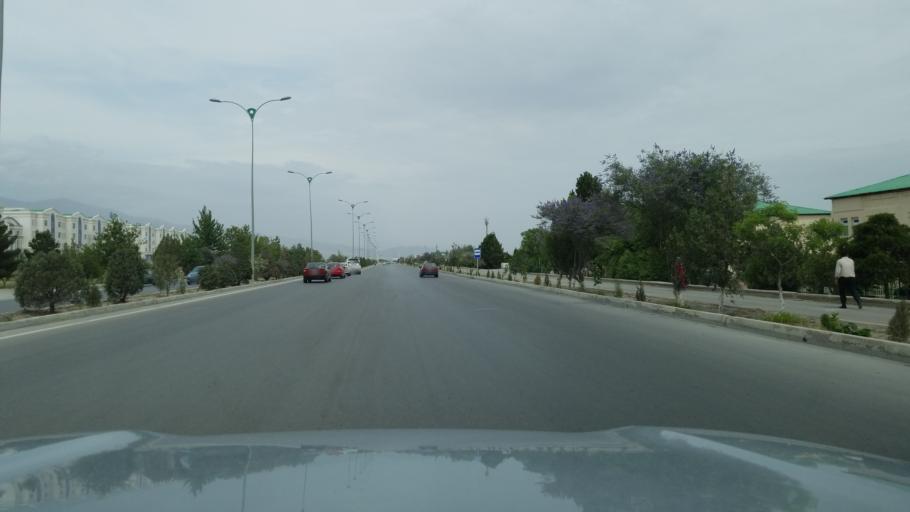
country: TM
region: Ahal
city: Abadan
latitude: 38.1655
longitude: 57.9360
